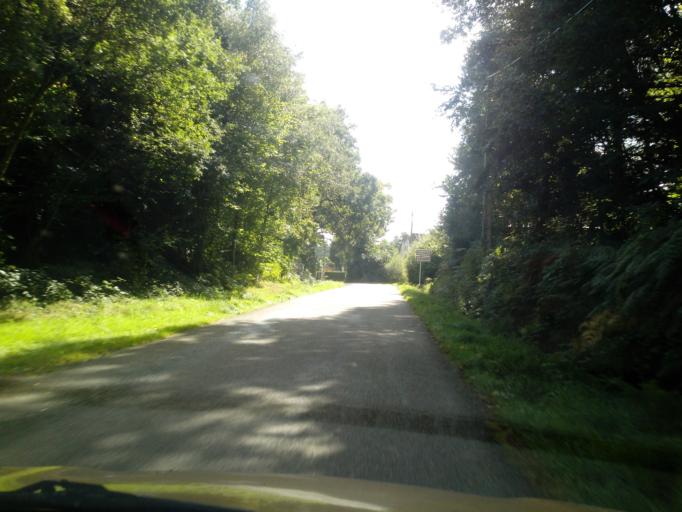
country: FR
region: Brittany
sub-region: Departement du Morbihan
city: Meneac
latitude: 48.1235
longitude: -2.3889
